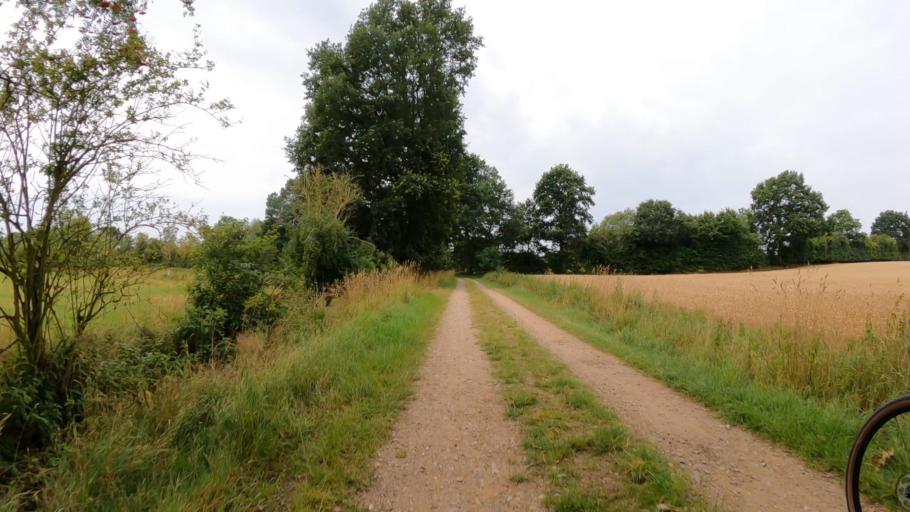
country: DE
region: Schleswig-Holstein
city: Seth
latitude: 53.8543
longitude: 10.2069
